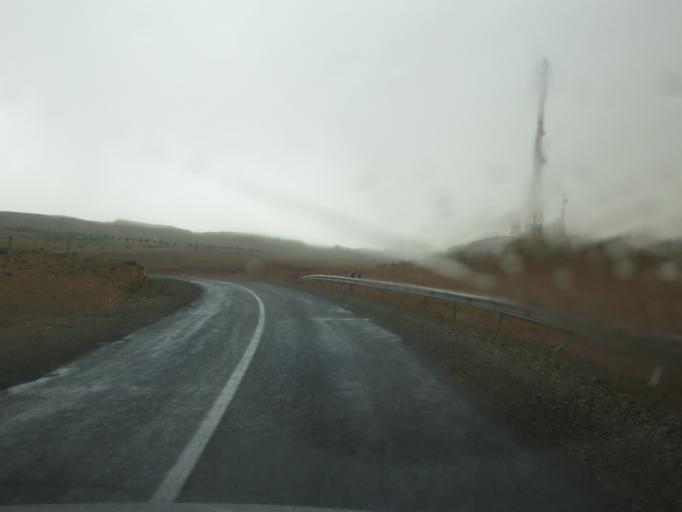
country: MA
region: Meknes-Tafilalet
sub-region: Khenifra
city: Midelt
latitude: 32.6813
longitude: -4.6570
